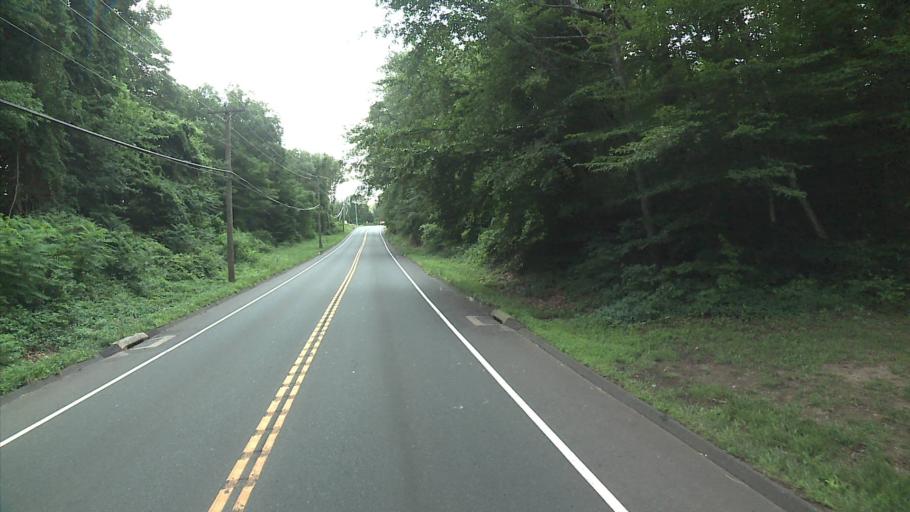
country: US
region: Connecticut
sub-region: Middlesex County
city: Portland
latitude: 41.5776
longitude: -72.6072
